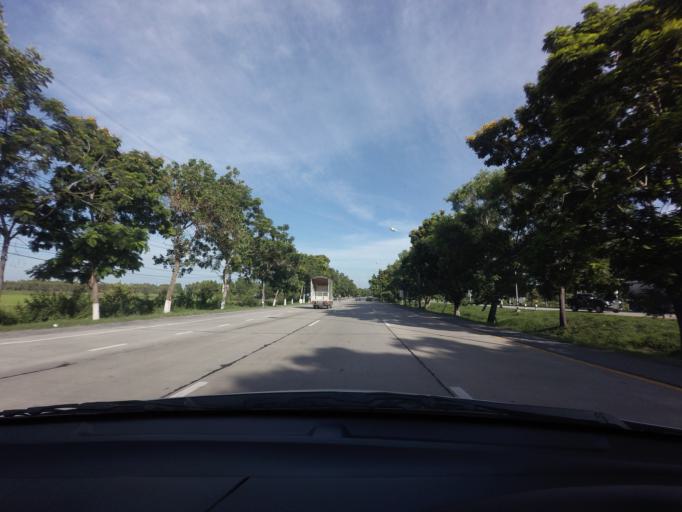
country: TH
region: Suphan Buri
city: Bang Pla Ma
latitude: 14.3882
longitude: 100.1744
